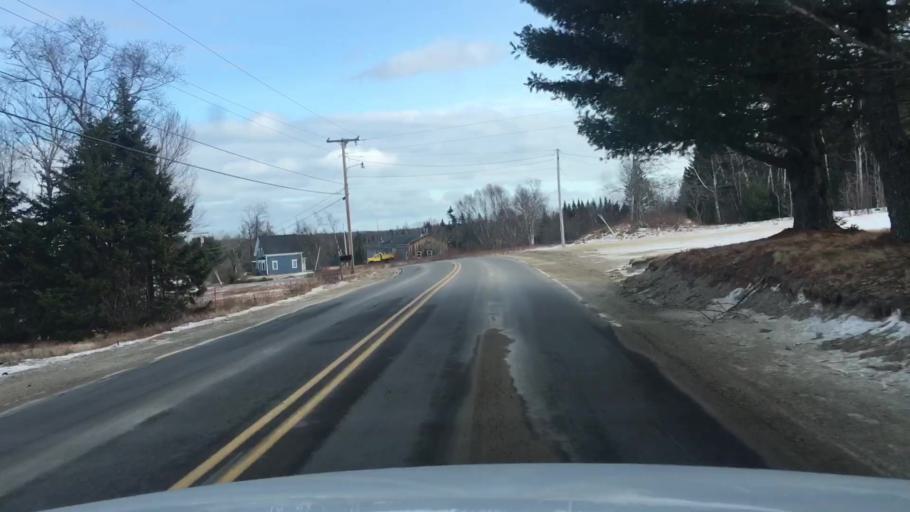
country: US
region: Maine
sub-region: Washington County
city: Jonesport
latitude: 44.6084
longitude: -67.5980
